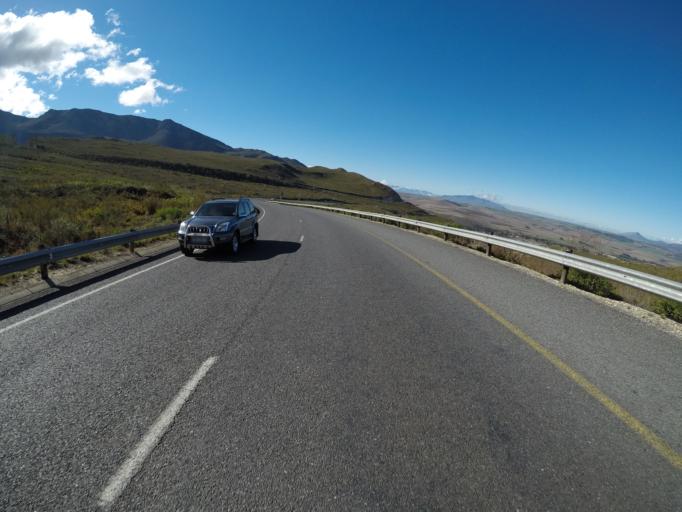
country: ZA
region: Western Cape
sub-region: Overberg District Municipality
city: Grabouw
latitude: -34.2239
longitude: 19.1738
